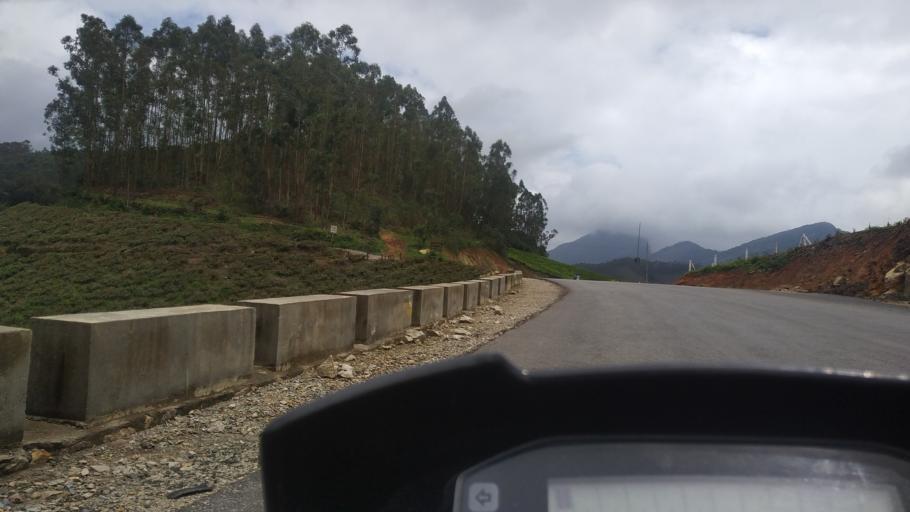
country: IN
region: Kerala
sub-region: Idukki
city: Munnar
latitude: 10.0788
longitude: 77.0866
